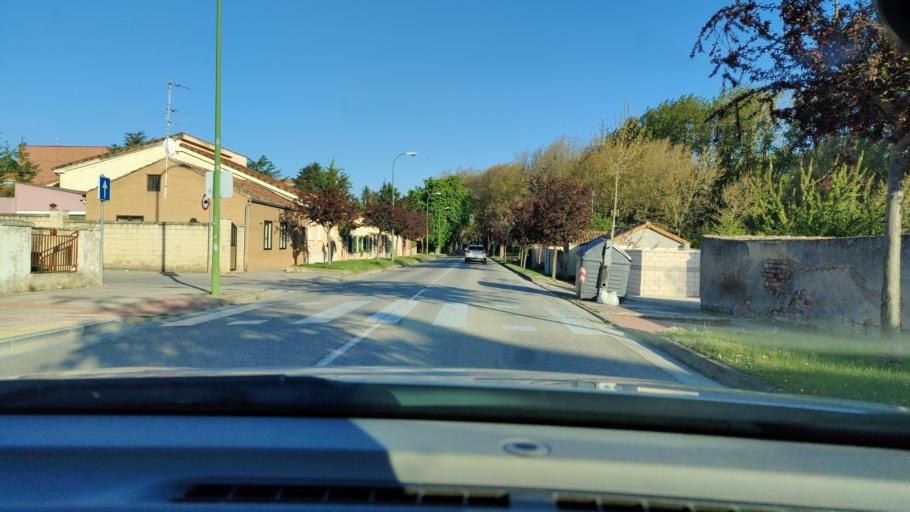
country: ES
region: Castille and Leon
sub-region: Provincia de Burgos
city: Villagonzalo-Pedernales
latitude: 42.3472
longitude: -3.7308
